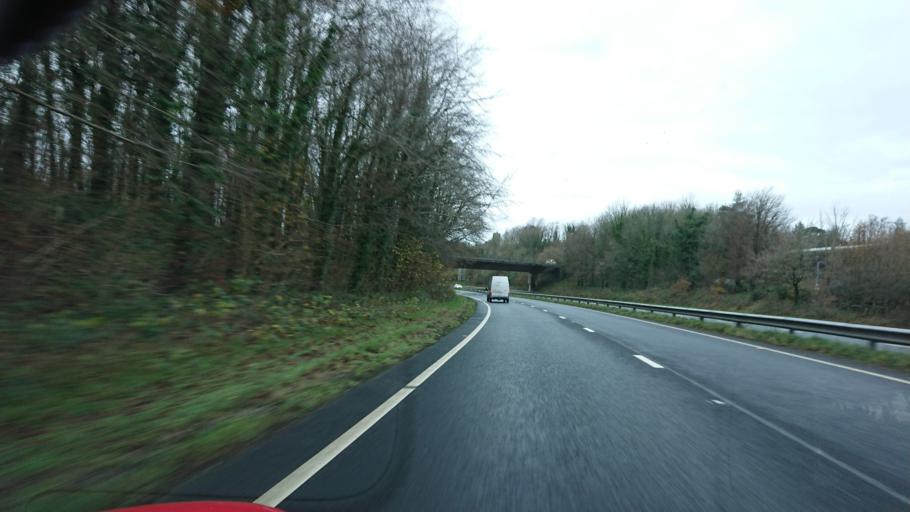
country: GB
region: England
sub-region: Cornwall
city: Liskeard
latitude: 50.4488
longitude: -4.4546
